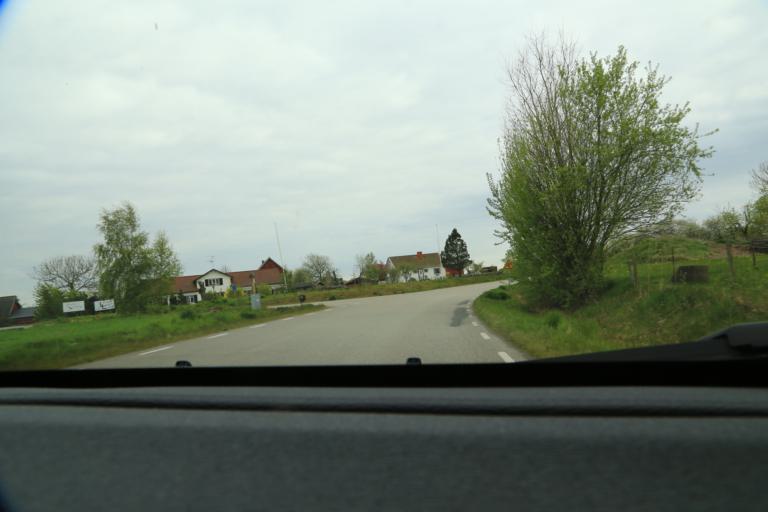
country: SE
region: Halland
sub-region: Varbergs Kommun
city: Tvaaker
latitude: 57.0432
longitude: 12.3638
